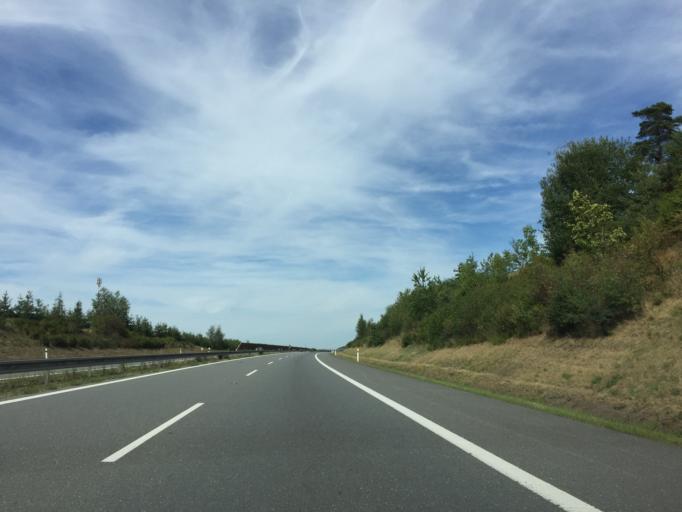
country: CZ
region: Jihocesky
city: Chotoviny
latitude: 49.4997
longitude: 14.6605
